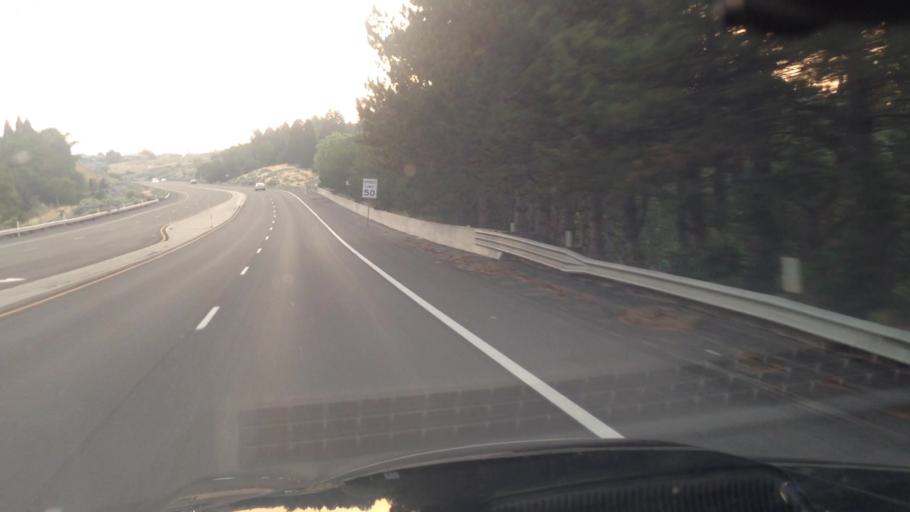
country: US
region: Nevada
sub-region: Washoe County
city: Reno
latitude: 39.4778
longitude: -119.8234
